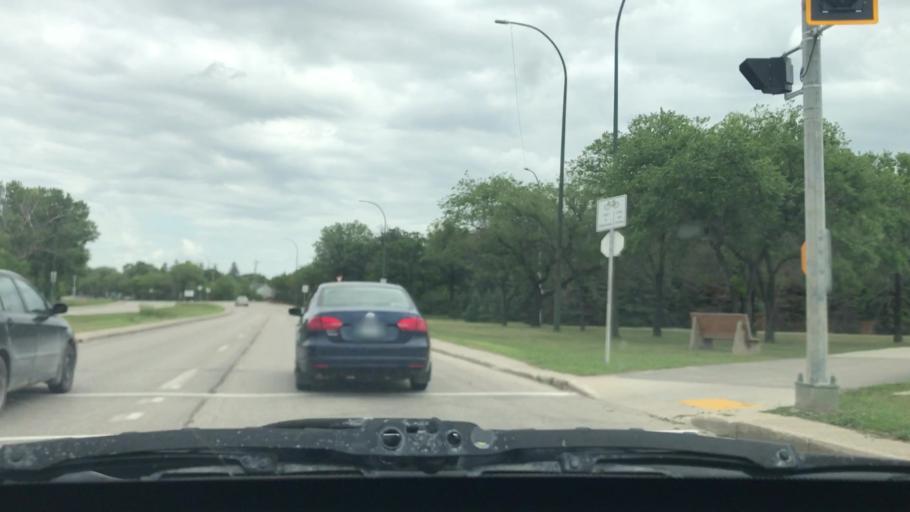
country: CA
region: Manitoba
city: Winnipeg
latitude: 49.8502
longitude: -97.1204
